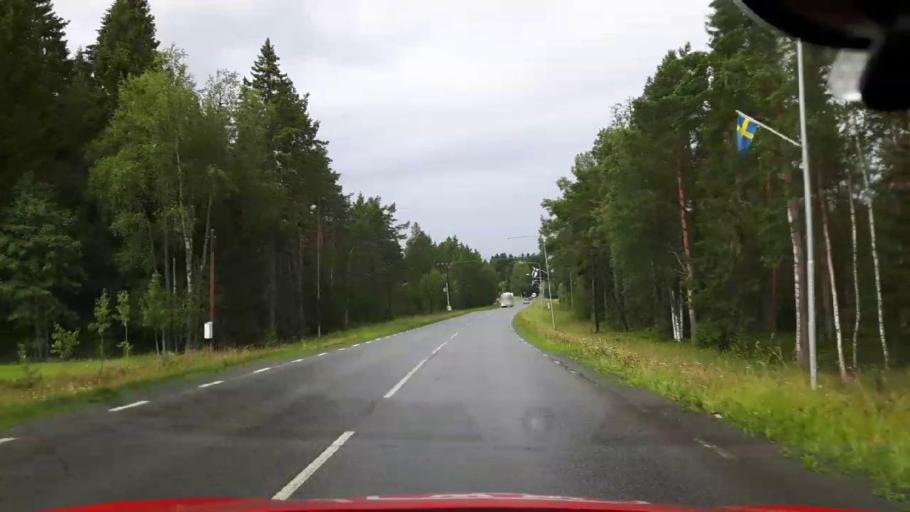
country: SE
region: Jaemtland
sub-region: Krokoms Kommun
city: Krokom
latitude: 63.3443
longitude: 14.2638
